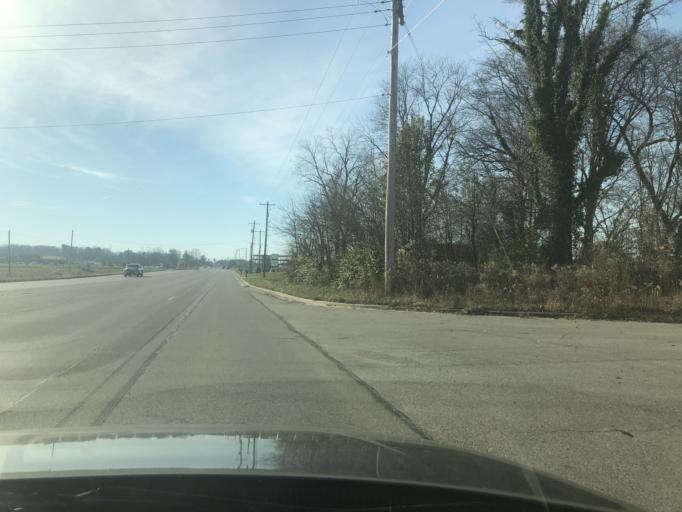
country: US
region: Indiana
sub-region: Warrick County
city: Newburgh
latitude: 37.9841
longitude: -87.4412
